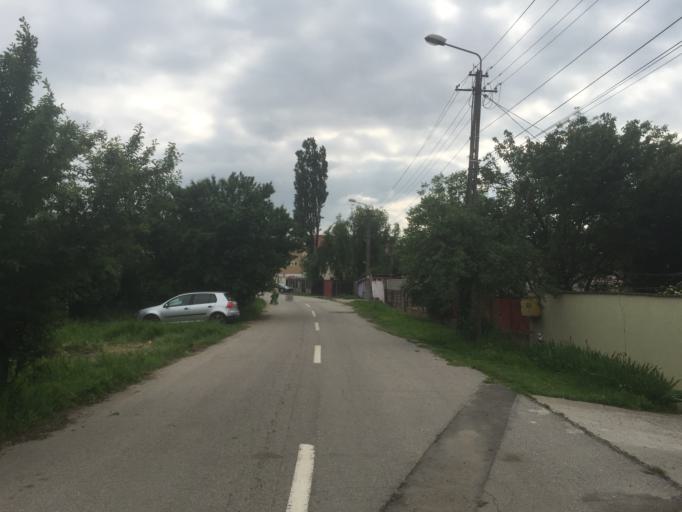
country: RO
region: Timis
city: Timisoara
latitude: 45.7566
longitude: 21.1975
